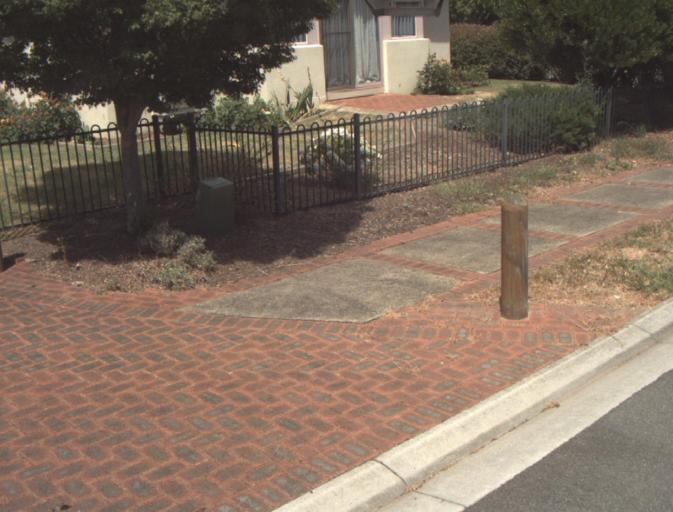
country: AU
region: Tasmania
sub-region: Launceston
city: Launceston
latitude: -41.4215
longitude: 147.1271
